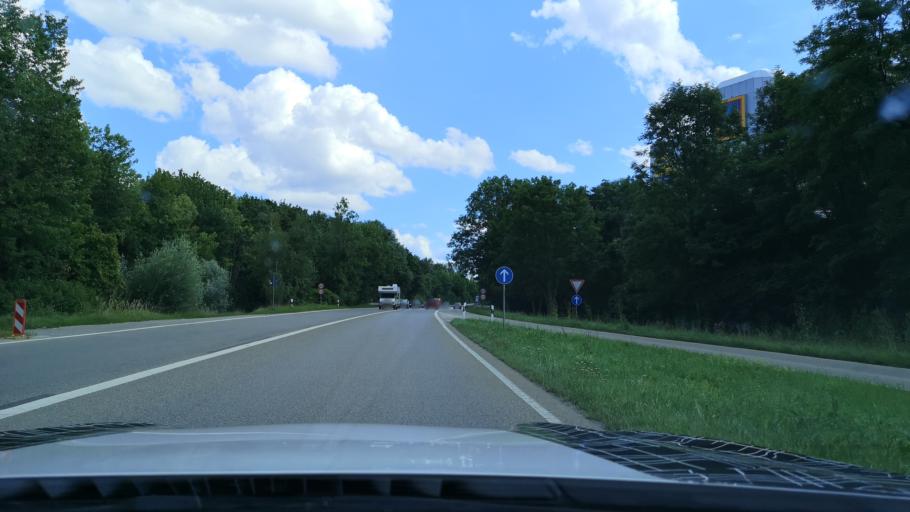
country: DE
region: Bavaria
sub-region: Upper Bavaria
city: Unterfoehring
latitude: 48.1799
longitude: 11.6354
